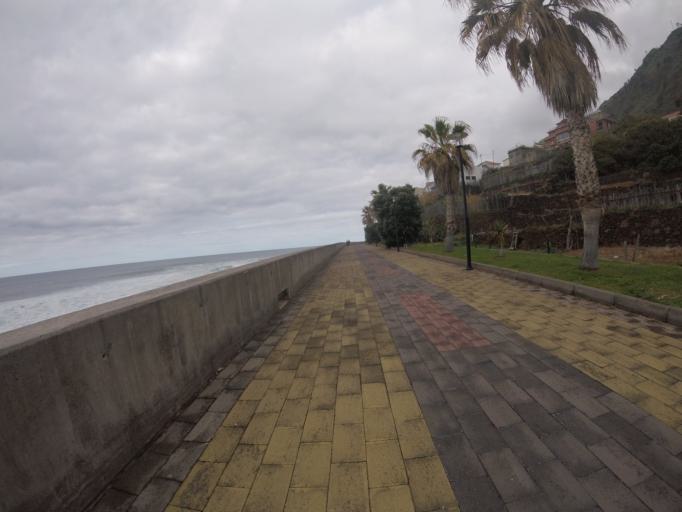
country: PT
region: Madeira
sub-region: Calheta
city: Estreito da Calheta
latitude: 32.7363
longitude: -17.2112
